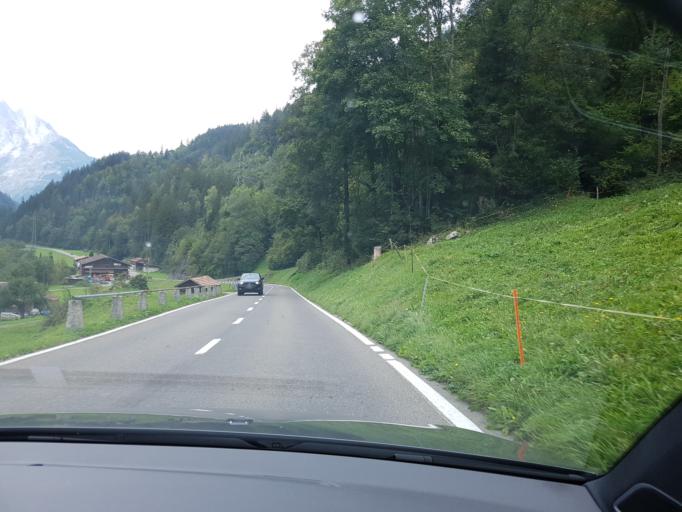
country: CH
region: Bern
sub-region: Interlaken-Oberhasli District
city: Meiringen
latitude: 46.7204
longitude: 8.2913
